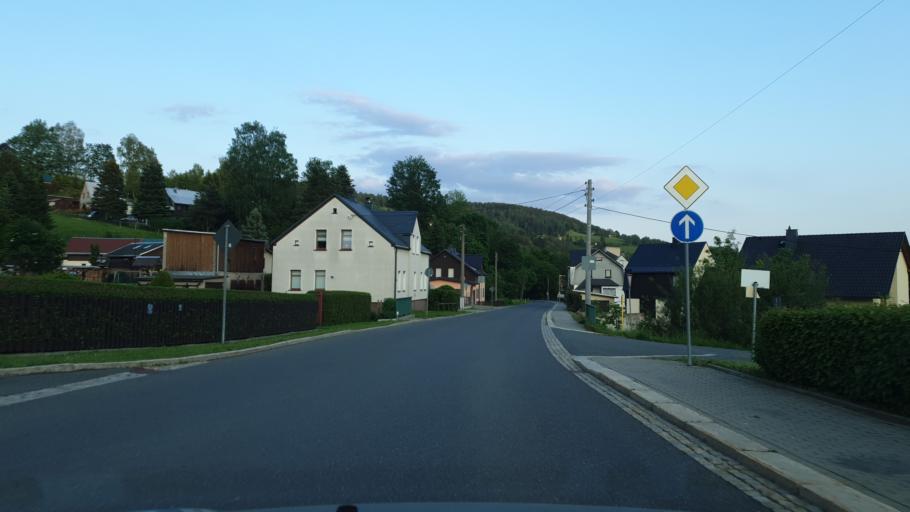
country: DE
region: Saxony
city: Klingenthal
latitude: 50.3777
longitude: 12.4648
